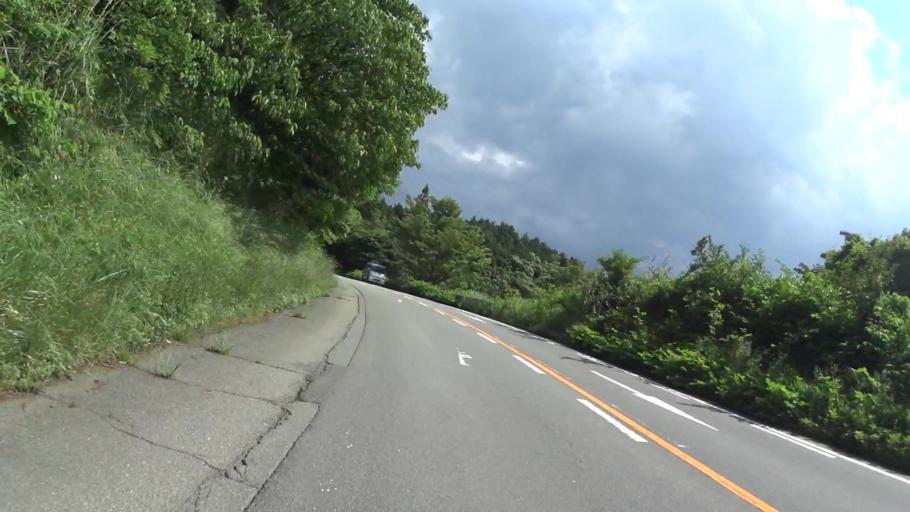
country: JP
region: Kumamoto
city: Aso
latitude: 33.0430
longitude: 131.1665
